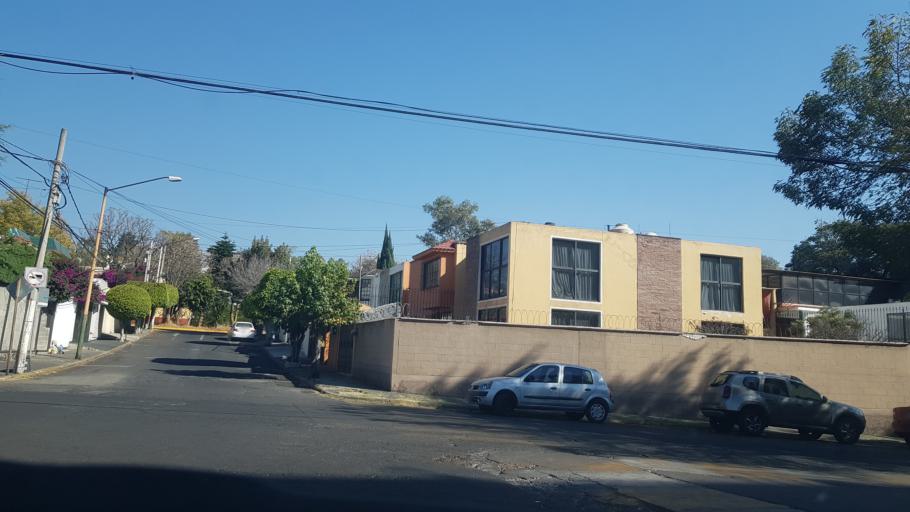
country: MX
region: Mexico
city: Naucalpan de Juarez
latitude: 19.4967
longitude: -99.2478
